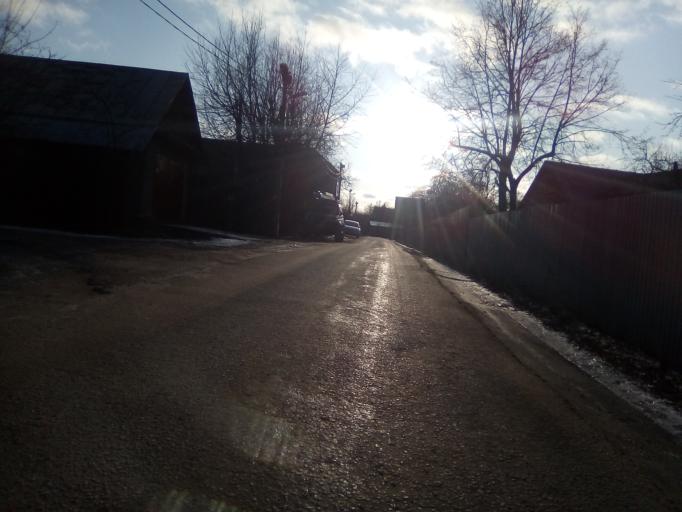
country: RU
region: Moskovskaya
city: Lesnoy Gorodok
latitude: 55.6699
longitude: 37.1790
